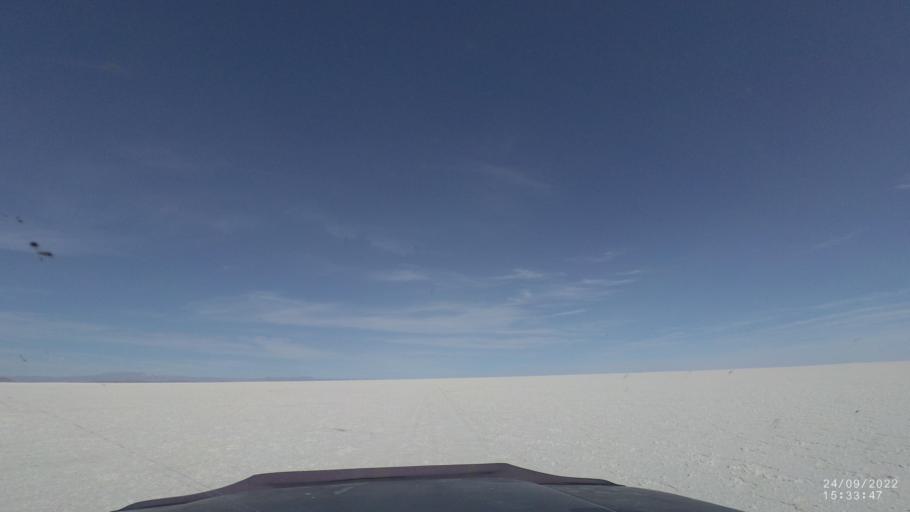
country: BO
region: Potosi
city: Colchani
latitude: -20.1183
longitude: -67.2682
